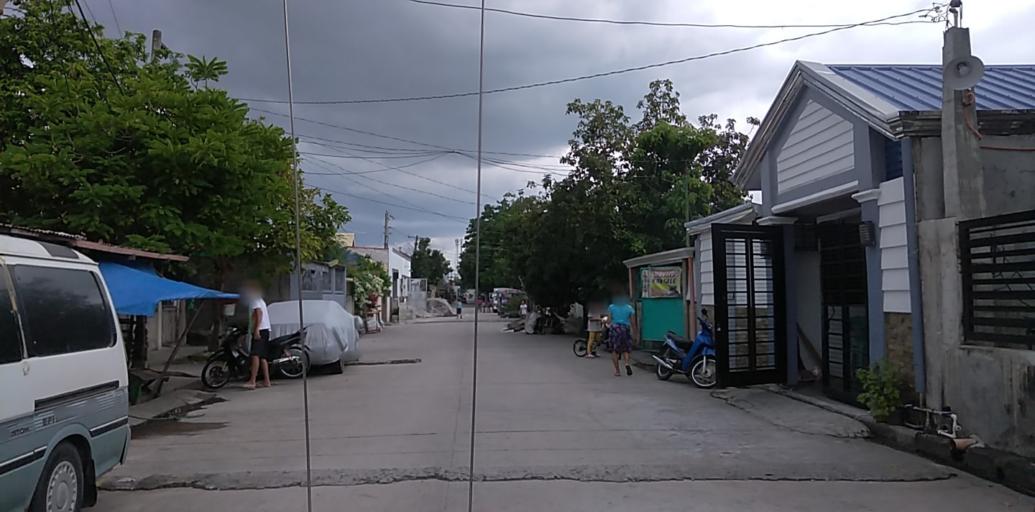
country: PH
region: Central Luzon
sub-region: Province of Pampanga
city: Pio
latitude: 15.0441
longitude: 120.5269
